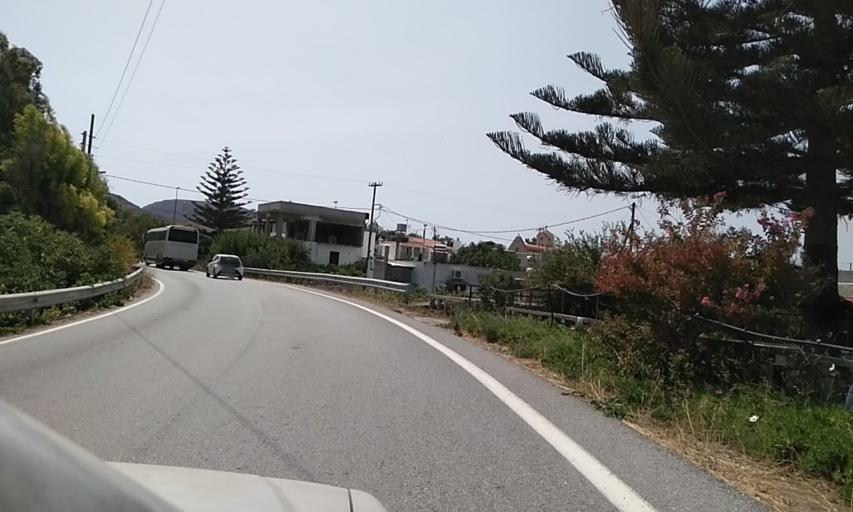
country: GR
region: Crete
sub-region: Nomos Lasithiou
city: Makry-Gialos
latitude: 35.1047
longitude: 26.0594
